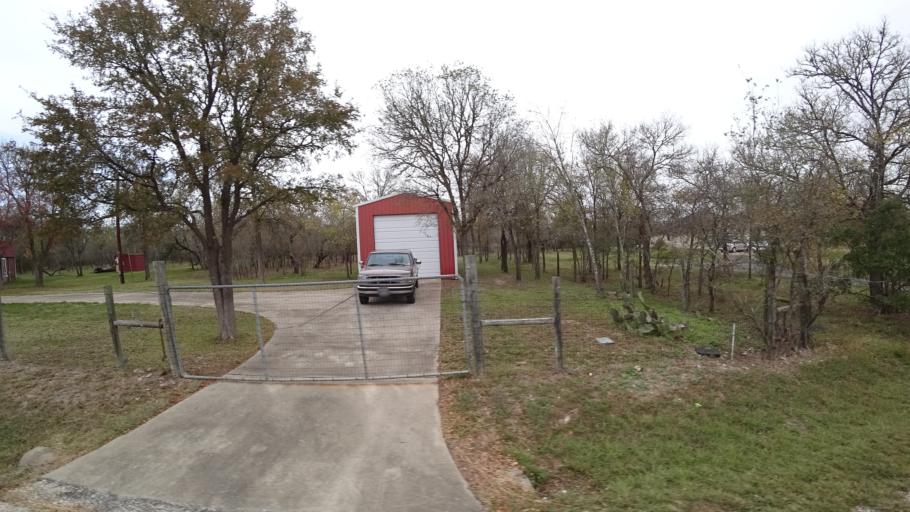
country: US
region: Texas
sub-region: Travis County
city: Garfield
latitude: 30.1053
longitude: -97.5725
